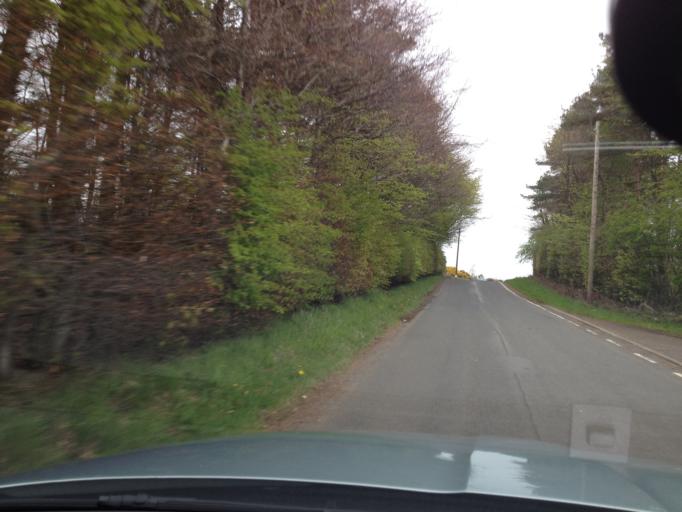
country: GB
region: Scotland
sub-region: West Lothian
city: Linlithgow
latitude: 55.9339
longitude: -3.6040
